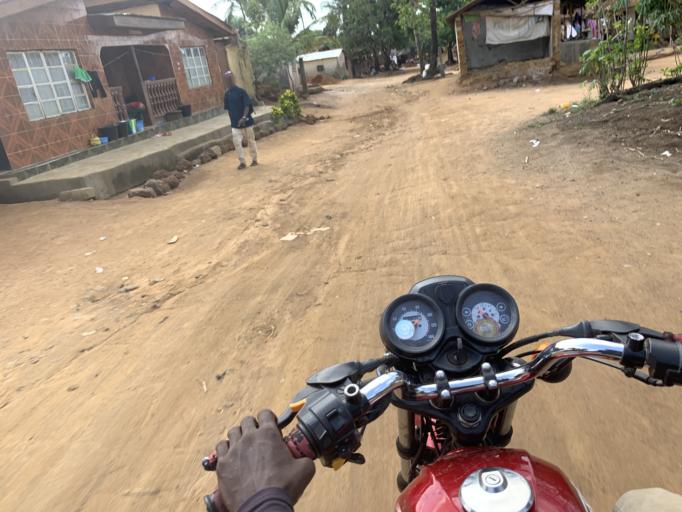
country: SL
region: Western Area
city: Waterloo
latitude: 8.3288
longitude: -13.0557
